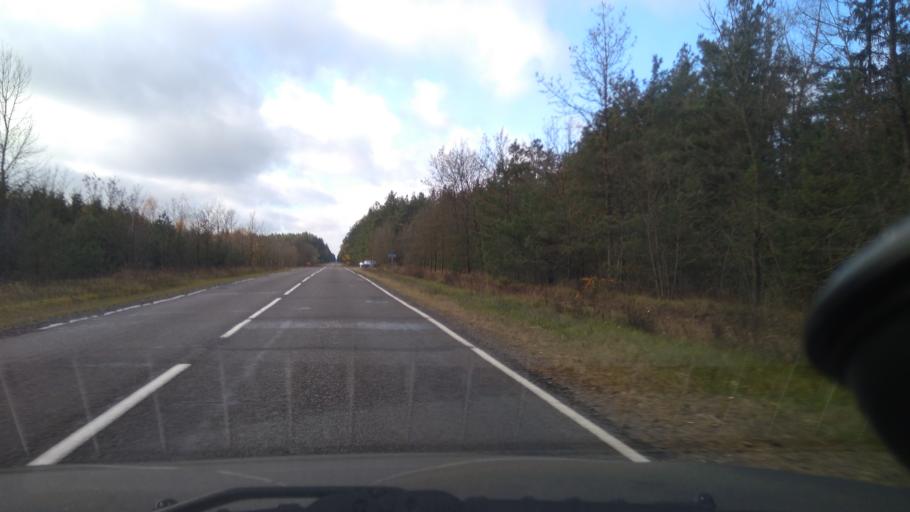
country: BY
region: Minsk
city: Slutsk
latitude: 53.2290
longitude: 27.7147
